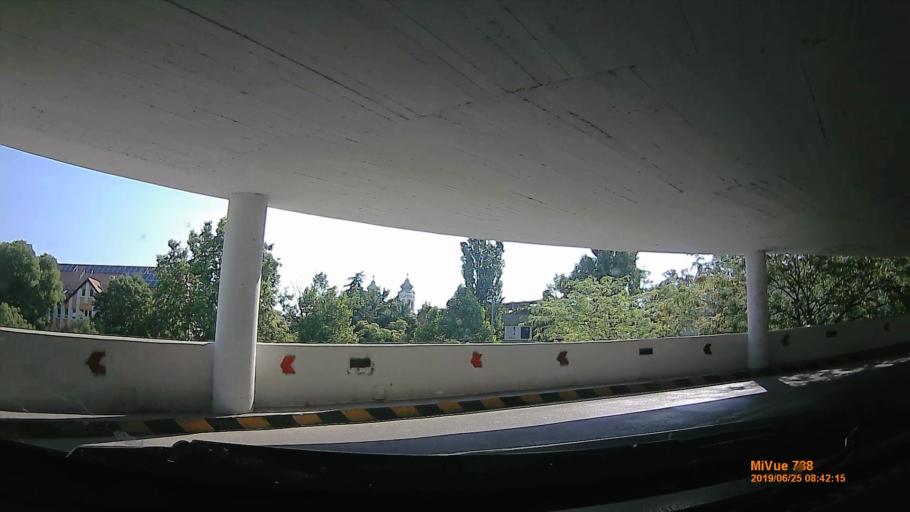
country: HU
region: Fejer
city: Szekesfehervar
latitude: 47.1916
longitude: 18.4059
